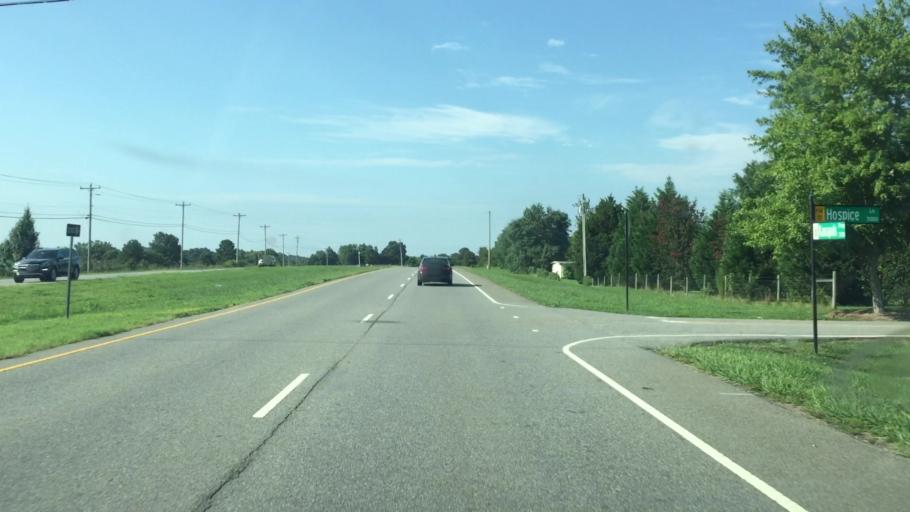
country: US
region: North Carolina
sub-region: Rowan County
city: Enochville
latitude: 35.4852
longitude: -80.6732
